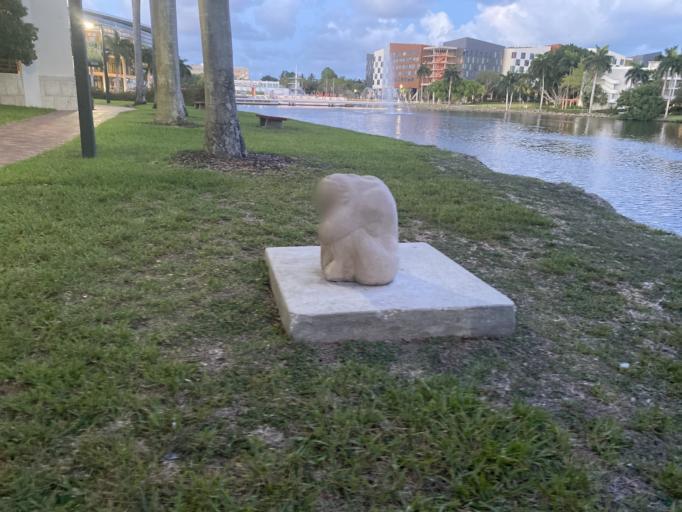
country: US
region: Florida
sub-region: Miami-Dade County
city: Coral Gables
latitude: 25.7183
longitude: -80.2805
